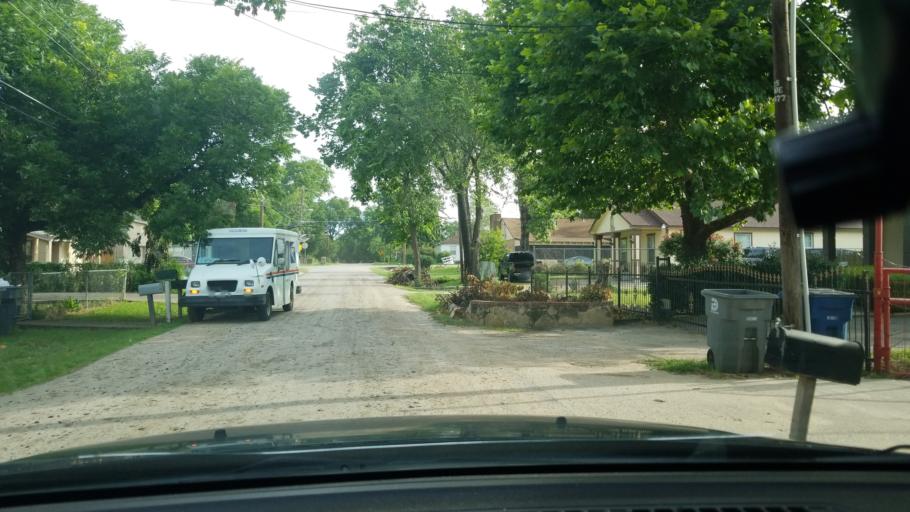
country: US
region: Texas
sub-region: Dallas County
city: Balch Springs
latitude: 32.7562
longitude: -96.6504
